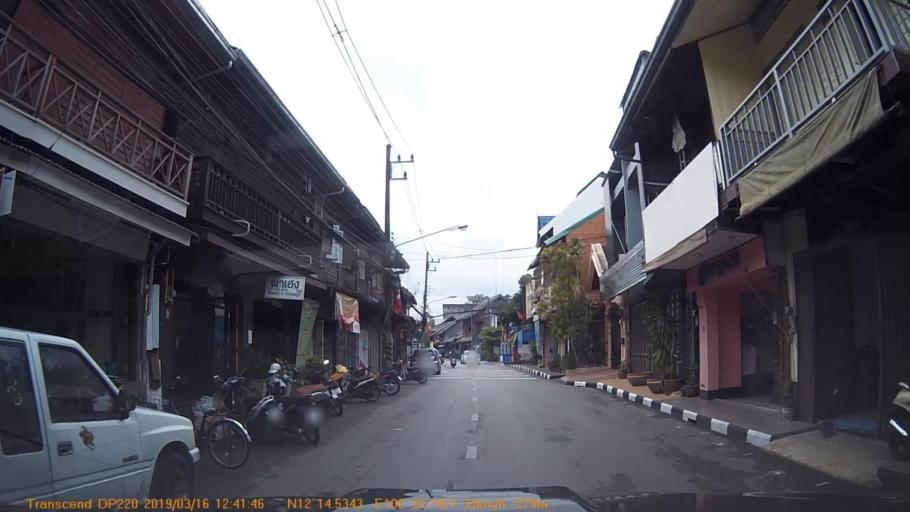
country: TH
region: Trat
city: Trat
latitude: 12.2423
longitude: 102.5123
